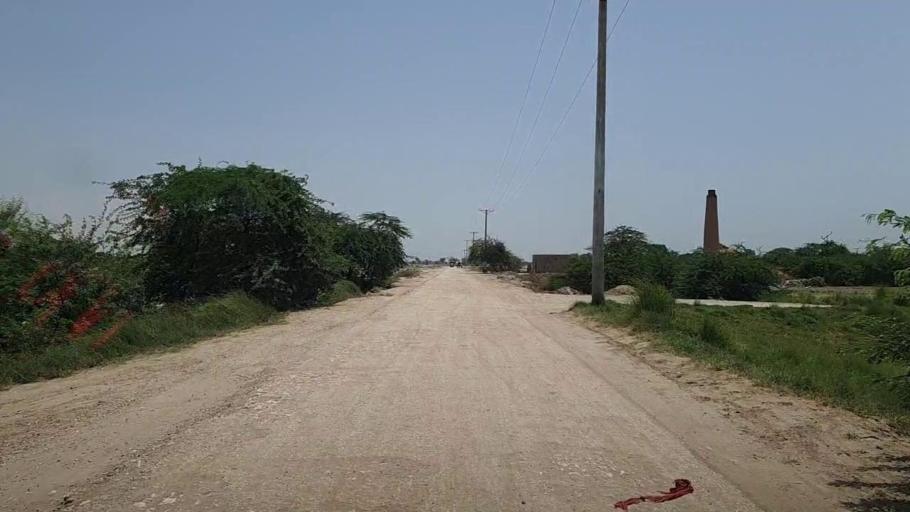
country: PK
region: Sindh
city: Pad Idan
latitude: 26.7703
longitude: 68.2921
